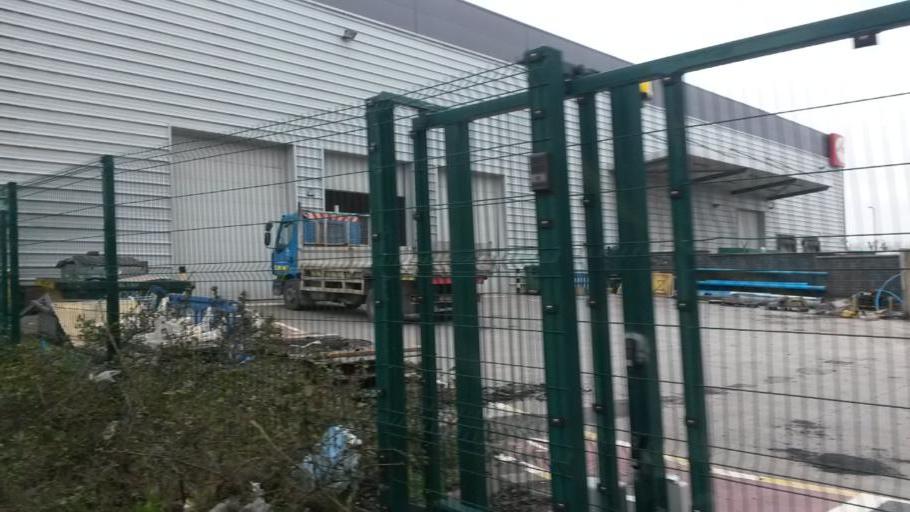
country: IE
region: Leinster
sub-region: Dublin City
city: Finglas
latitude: 53.3979
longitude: -6.3217
